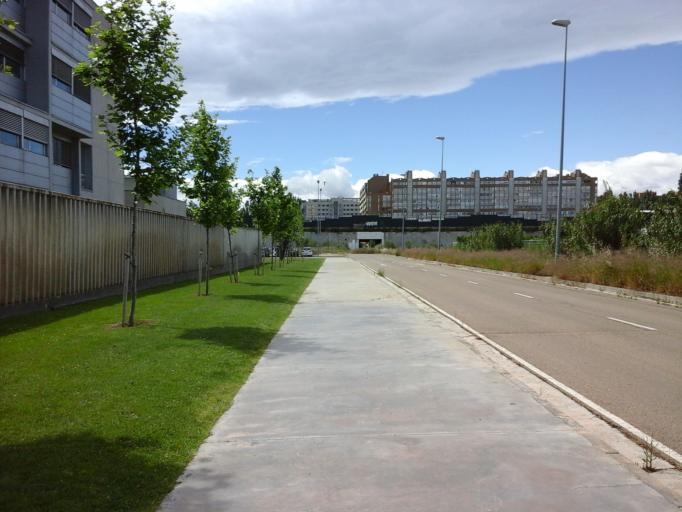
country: ES
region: Aragon
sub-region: Provincia de Zaragoza
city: Zaragoza
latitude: 41.6820
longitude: -0.8838
